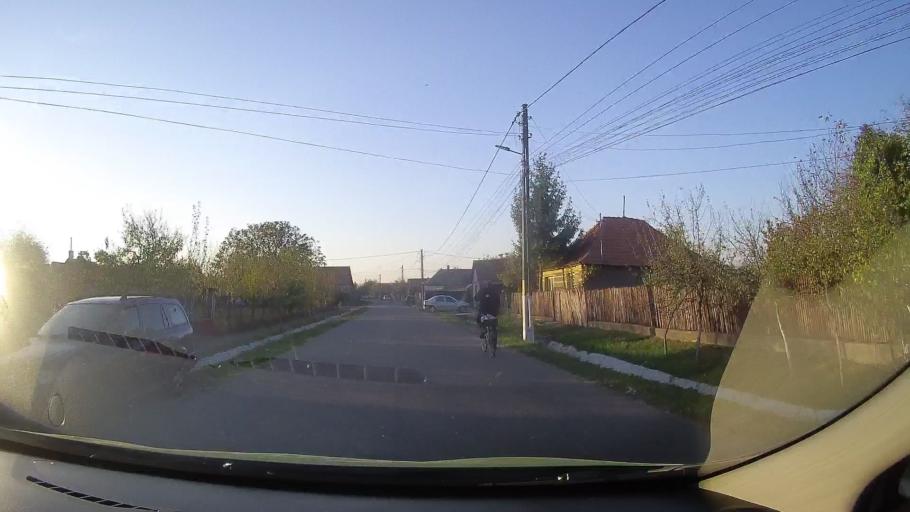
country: RO
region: Bihor
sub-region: Comuna Salard
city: Salard
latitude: 47.2214
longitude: 22.0372
